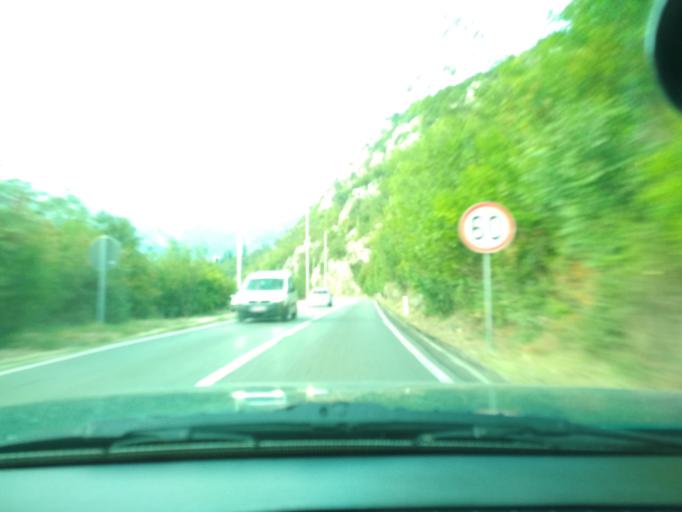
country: ME
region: Kotor
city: Risan
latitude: 42.4967
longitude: 18.6913
